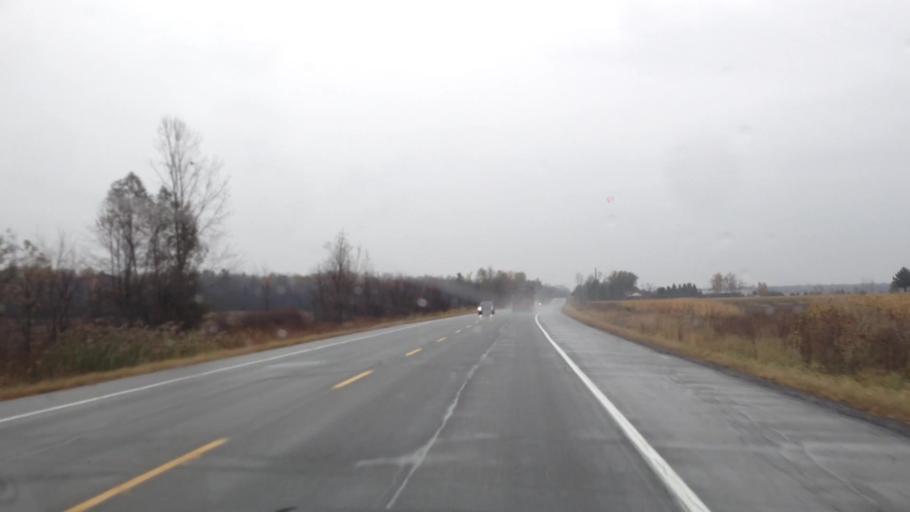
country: CA
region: Ontario
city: Clarence-Rockland
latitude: 45.3862
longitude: -75.3879
